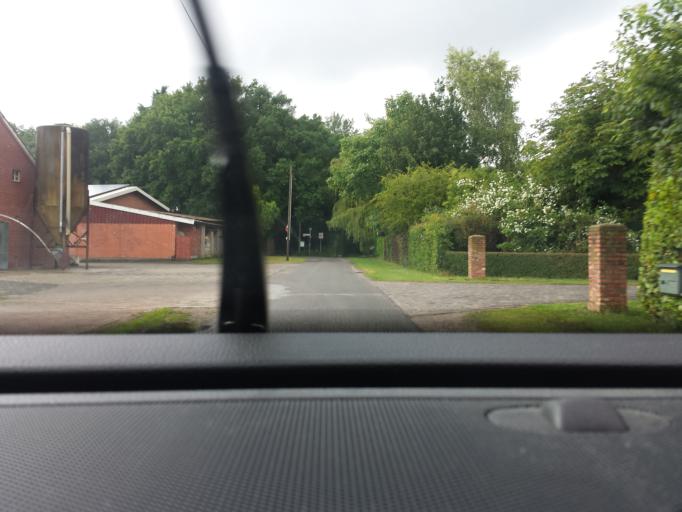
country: NL
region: Overijssel
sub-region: Gemeente Haaksbergen
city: Haaksbergen
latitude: 52.0748
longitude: 6.7373
